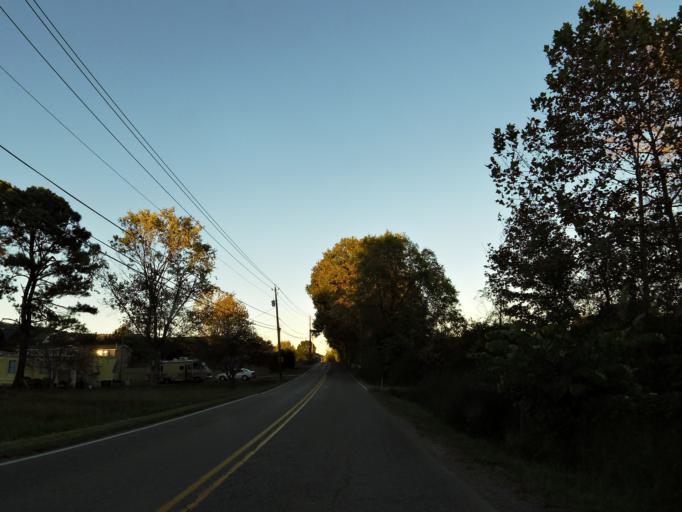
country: US
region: Tennessee
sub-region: Knox County
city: Knoxville
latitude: 36.0323
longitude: -83.9831
